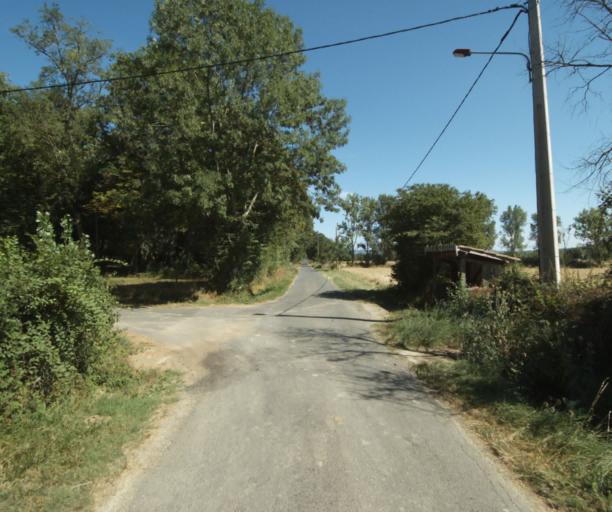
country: FR
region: Midi-Pyrenees
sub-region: Departement de la Haute-Garonne
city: Auriac-sur-Vendinelle
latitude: 43.5212
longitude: 1.8902
